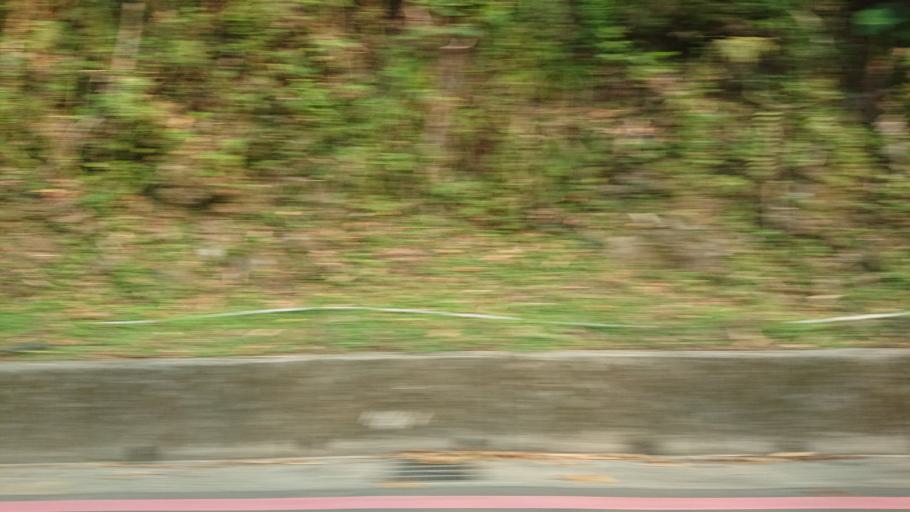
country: TW
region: Taiwan
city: Daxi
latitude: 24.8727
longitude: 121.3881
